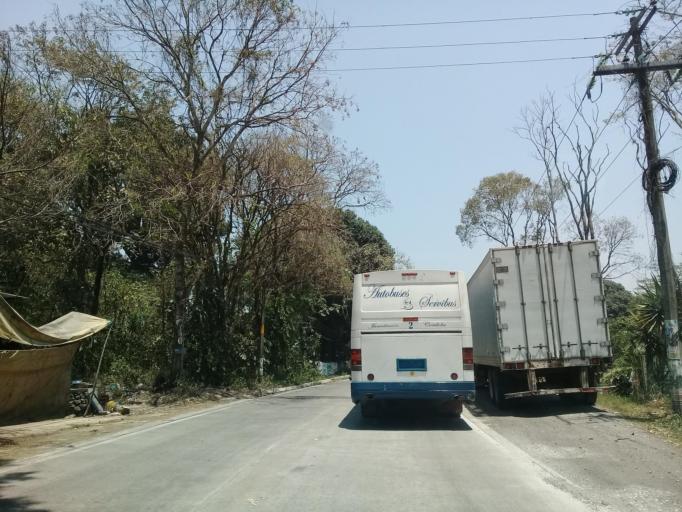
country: MX
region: Veracruz
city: Paraje Nuevo
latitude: 18.8721
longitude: -96.8752
